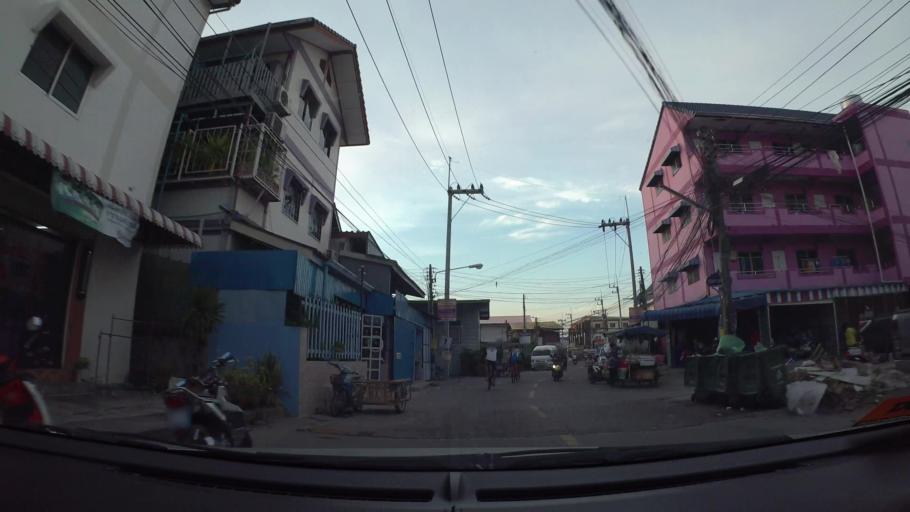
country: TH
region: Chon Buri
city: Chon Buri
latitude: 13.3952
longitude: 100.9858
